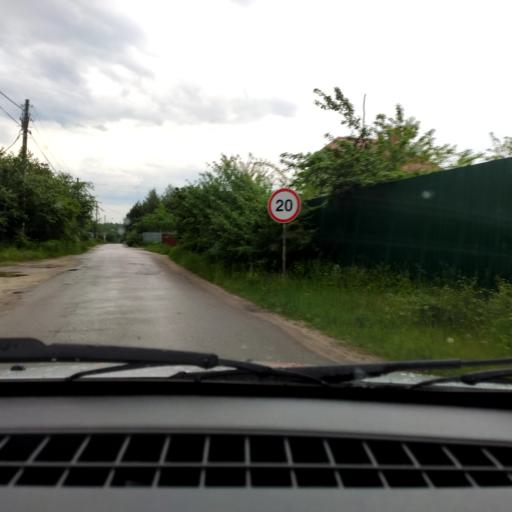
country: RU
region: Voronezj
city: Ramon'
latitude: 51.8577
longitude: 39.2497
